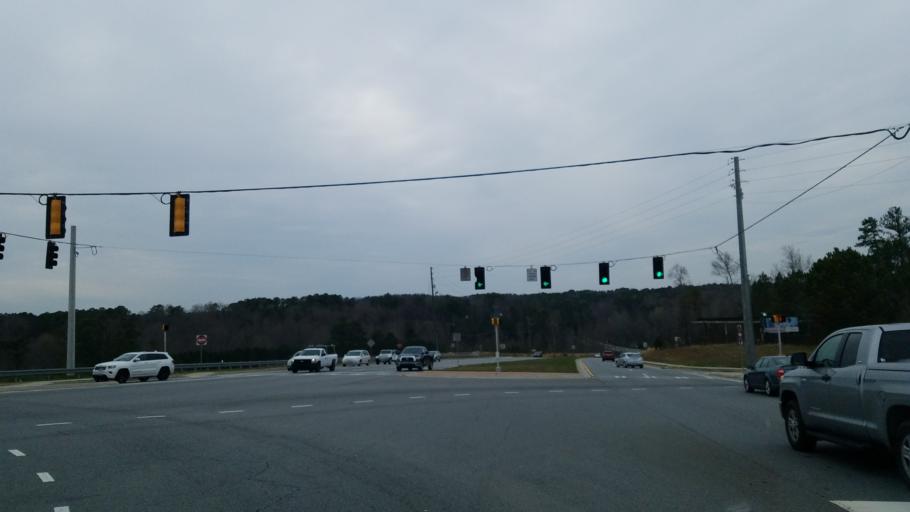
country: US
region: Georgia
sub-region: Cherokee County
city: Holly Springs
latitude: 34.1471
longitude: -84.5178
